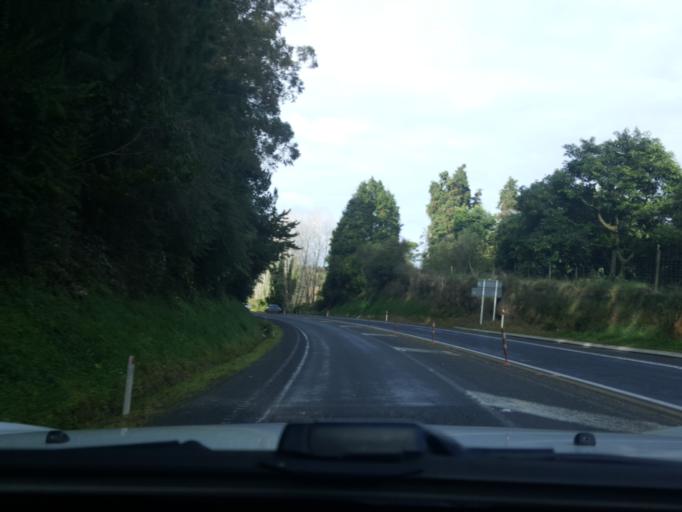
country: NZ
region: Bay of Plenty
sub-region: Tauranga City
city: Tauranga
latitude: -37.6822
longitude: 176.0267
